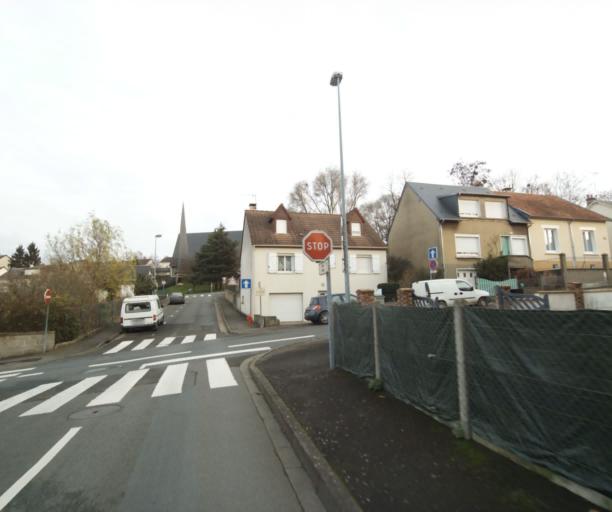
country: FR
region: Pays de la Loire
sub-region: Departement de la Sarthe
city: Coulaines
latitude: 48.0177
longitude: 0.2086
